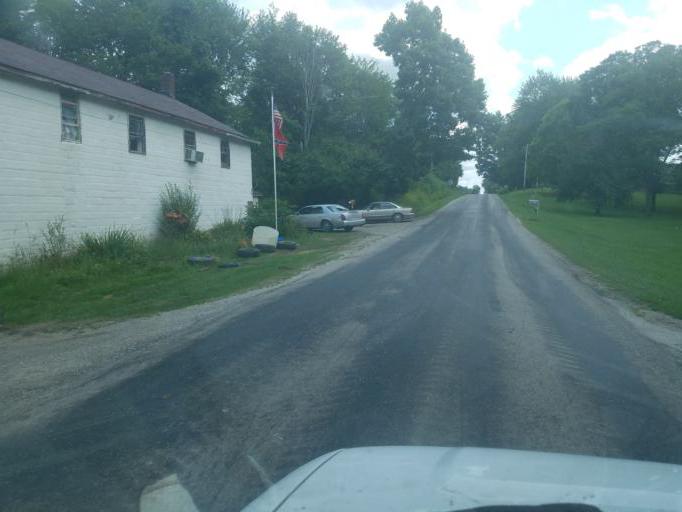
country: US
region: Ohio
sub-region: Ashtabula County
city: Roaming Shores
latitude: 41.5861
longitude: -80.7905
